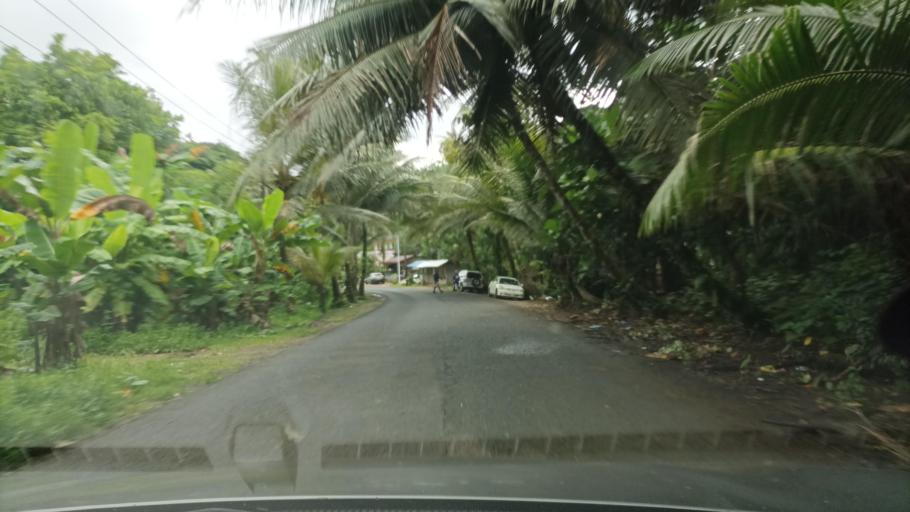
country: FM
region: Pohnpei
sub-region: Kolonia Municipality
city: Kolonia
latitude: 6.9519
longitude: 158.2328
